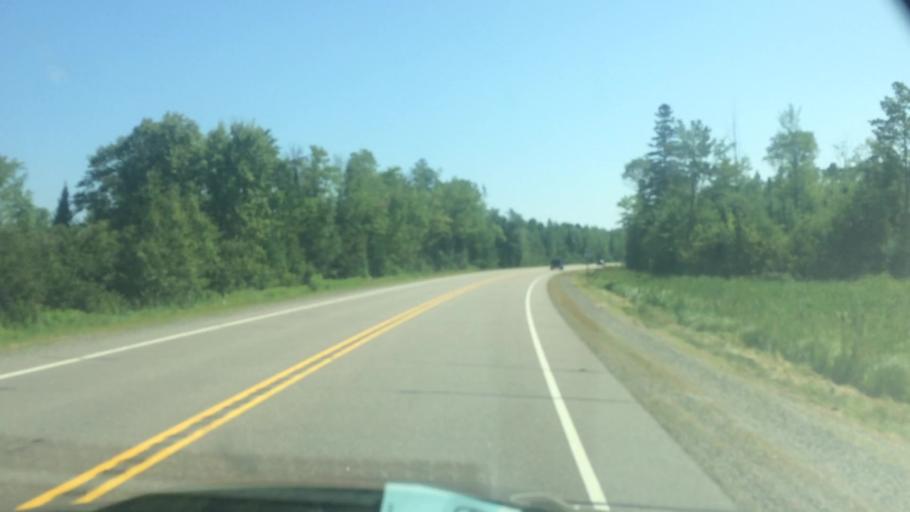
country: US
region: Wisconsin
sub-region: Lincoln County
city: Tomahawk
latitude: 45.5673
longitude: -89.6386
